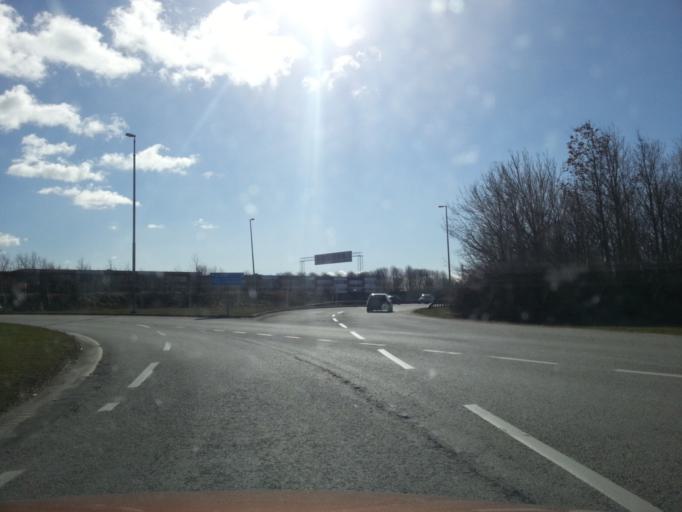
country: SE
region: Skane
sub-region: Lunds Kommun
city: Lund
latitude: 55.7149
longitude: 13.1627
